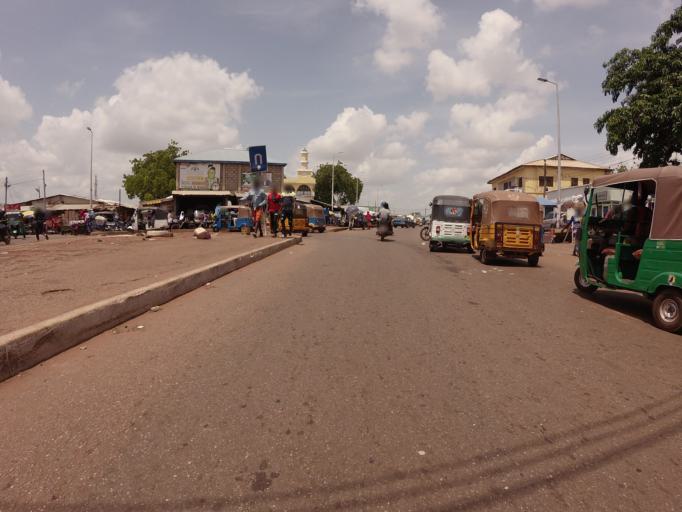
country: GH
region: Northern
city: Tamale
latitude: 9.4042
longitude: -0.8441
